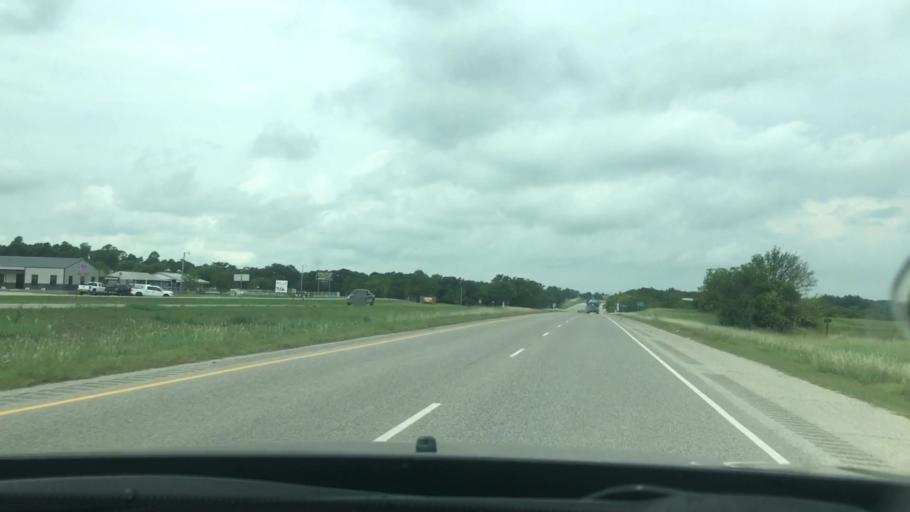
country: US
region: Oklahoma
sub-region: Carter County
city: Wilson
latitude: 34.1730
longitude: -97.4138
